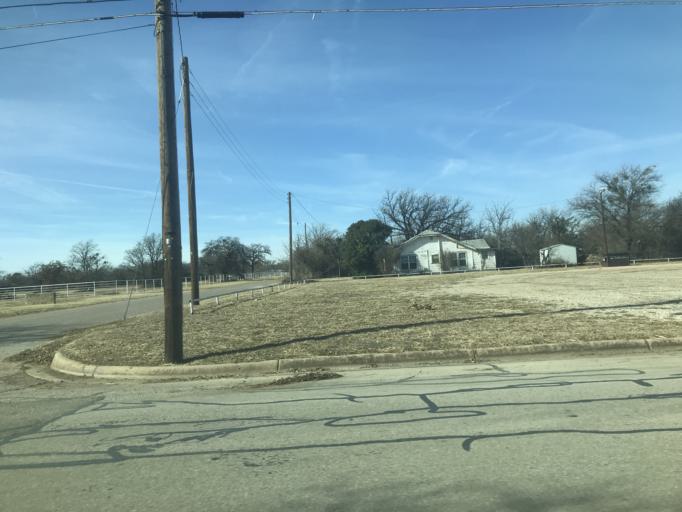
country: US
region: Texas
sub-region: Taylor County
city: Abilene
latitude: 32.4858
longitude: -99.7394
